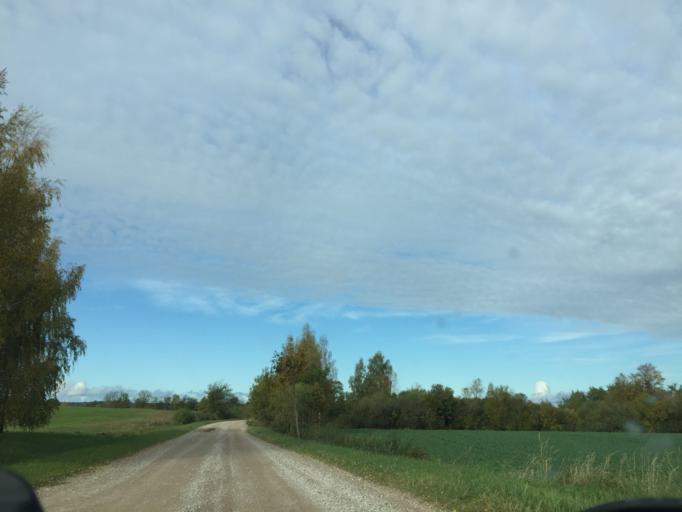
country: LV
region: Jaunpils
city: Jaunpils
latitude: 56.6194
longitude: 23.0668
